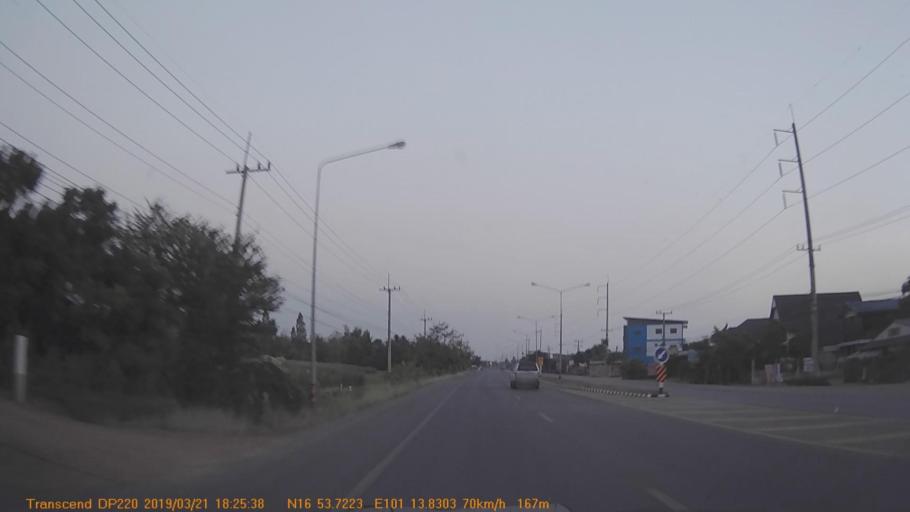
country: TH
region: Phetchabun
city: Lom Kao
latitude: 16.8952
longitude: 101.2305
